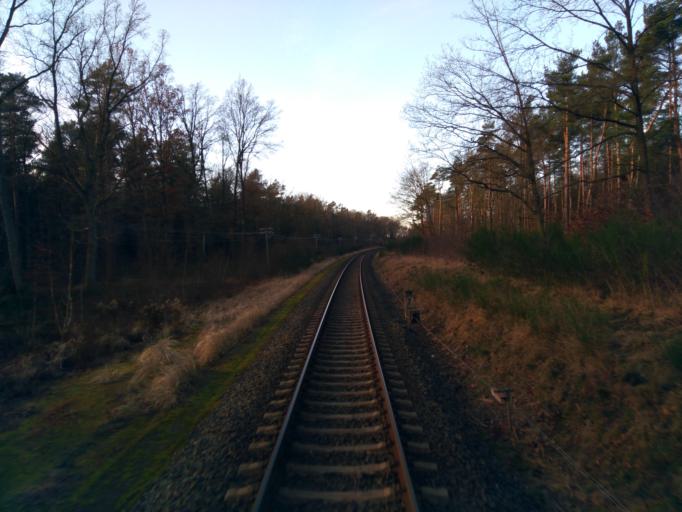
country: DE
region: Lower Saxony
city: Munster
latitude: 52.9897
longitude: 10.1232
